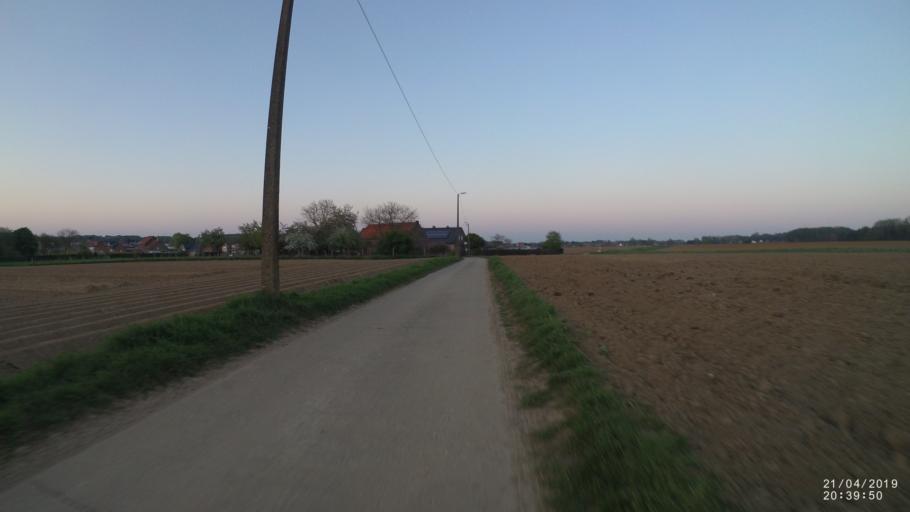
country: BE
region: Flanders
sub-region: Provincie Vlaams-Brabant
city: Lubbeek
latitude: 50.9010
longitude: 4.8569
